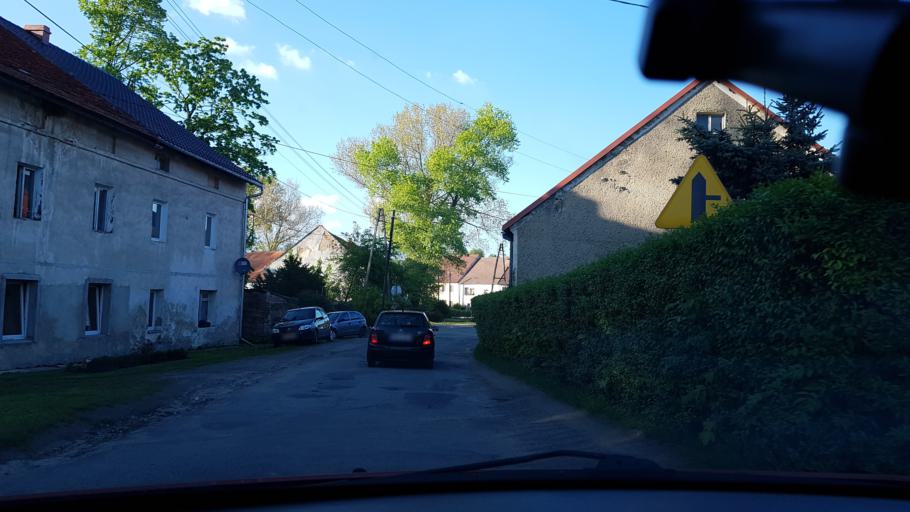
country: PL
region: Lower Silesian Voivodeship
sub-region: Powiat zabkowicki
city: Budzow
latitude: 50.6108
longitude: 16.6747
